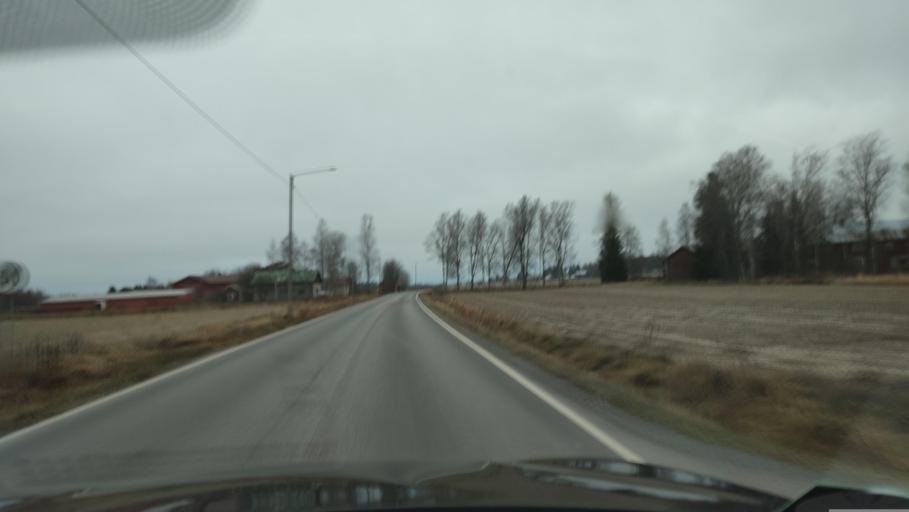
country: FI
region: Southern Ostrobothnia
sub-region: Suupohja
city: Karijoki
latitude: 62.2814
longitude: 21.7106
